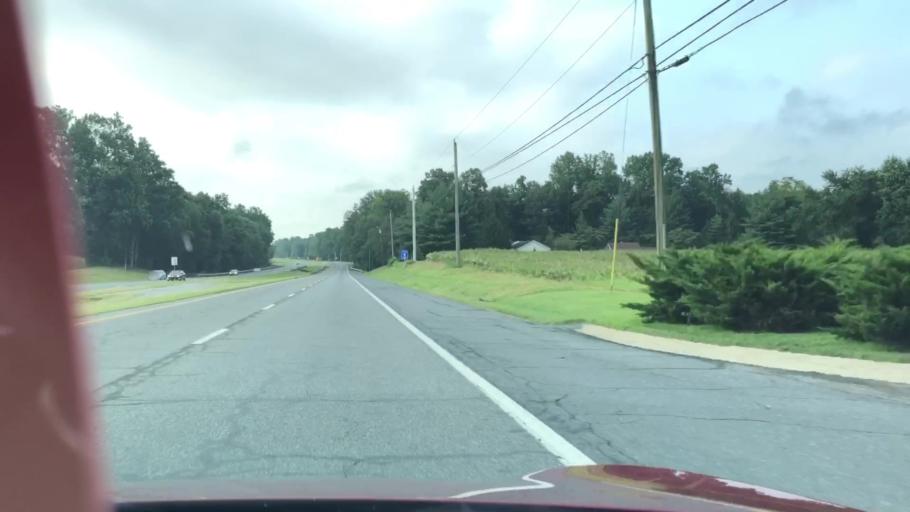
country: US
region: Delaware
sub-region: Kent County
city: Felton
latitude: 38.9789
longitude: -75.5674
